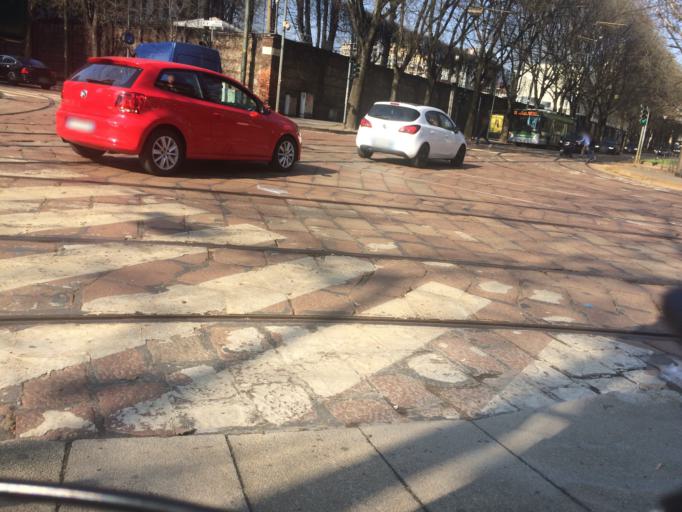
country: IT
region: Lombardy
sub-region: Citta metropolitana di Milano
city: Milano
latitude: 45.4722
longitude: 9.1673
